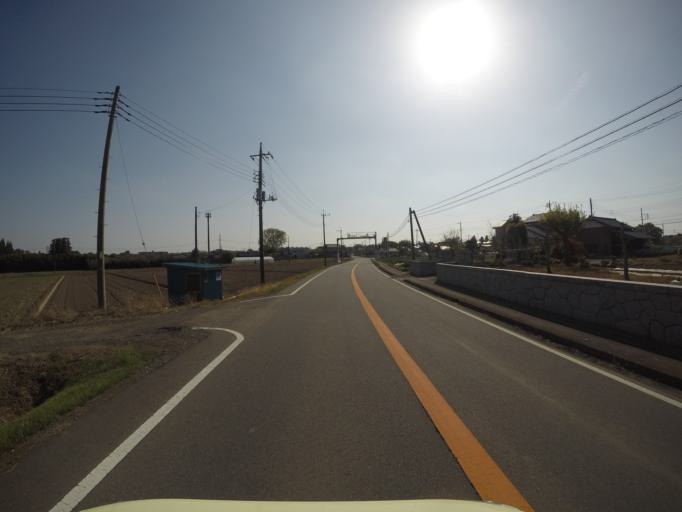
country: JP
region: Ibaraki
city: Yuki
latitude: 36.3125
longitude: 139.8818
